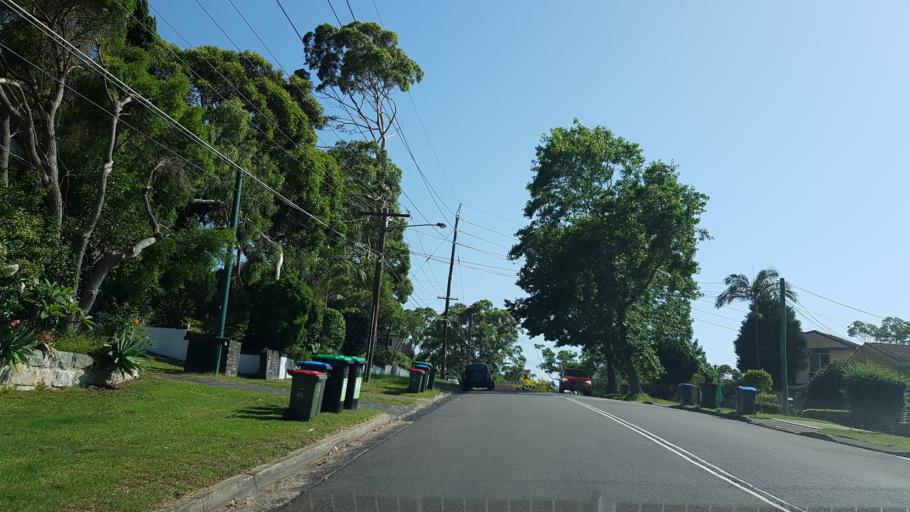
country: AU
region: New South Wales
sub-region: Warringah
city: Narraweena
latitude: -33.7367
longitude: 151.2712
